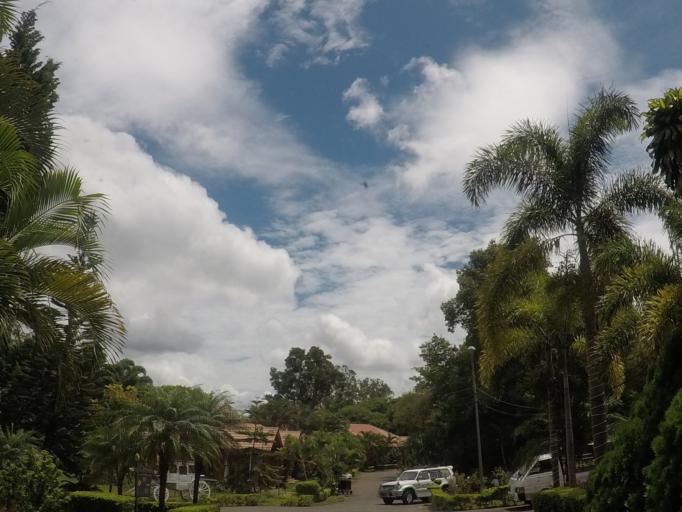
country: MM
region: Mandalay
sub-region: Pyin Oo Lwin District
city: Pyin Oo Lwin
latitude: 22.0223
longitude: 96.4579
